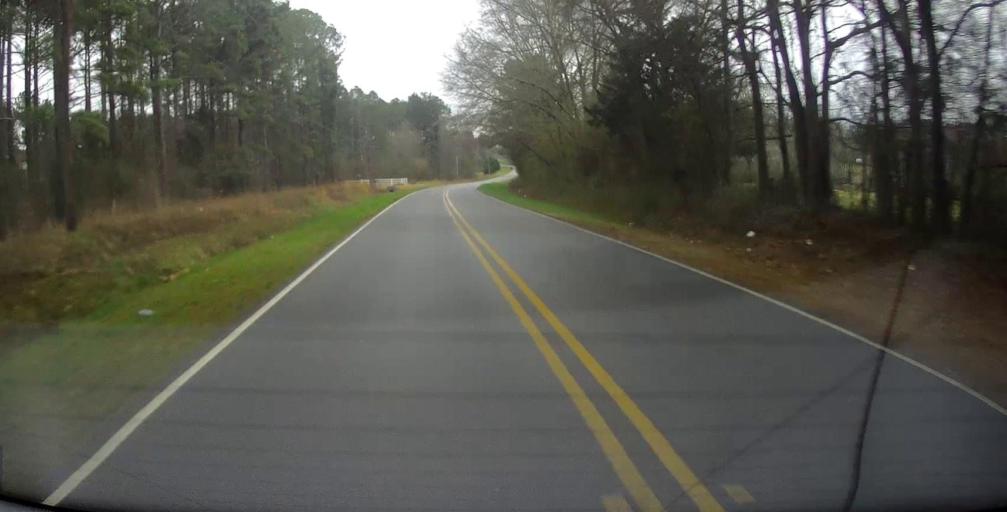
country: US
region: Georgia
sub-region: Pike County
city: Zebulon
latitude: 33.0714
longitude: -84.3279
